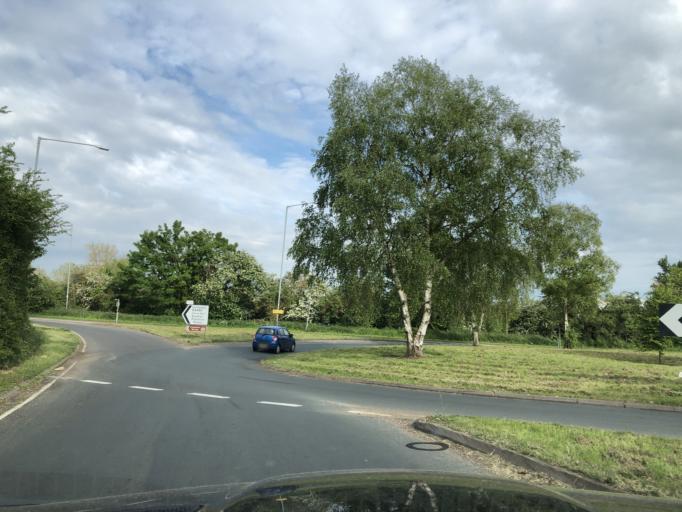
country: GB
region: England
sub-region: Warwickshire
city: Shipston on Stour
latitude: 52.1130
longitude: -1.6173
